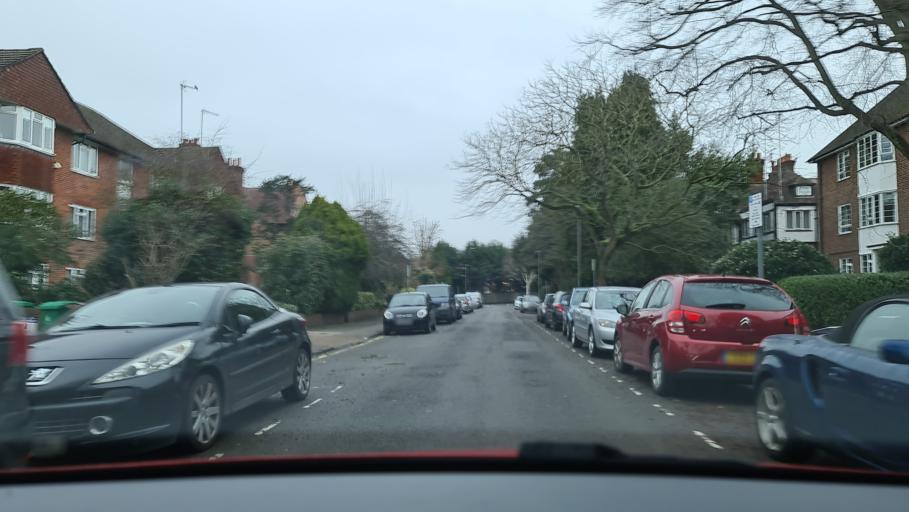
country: GB
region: England
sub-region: Greater London
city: Surbiton
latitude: 51.3887
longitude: -0.3070
